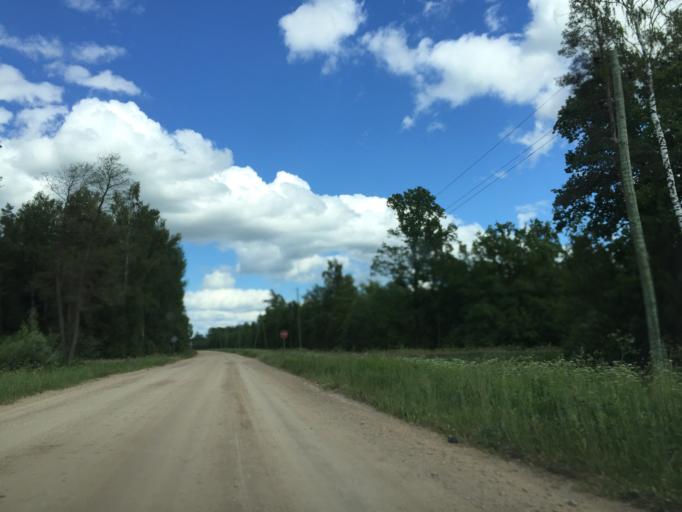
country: LV
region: Vecumnieki
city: Vecumnieki
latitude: 56.5040
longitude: 24.3865
